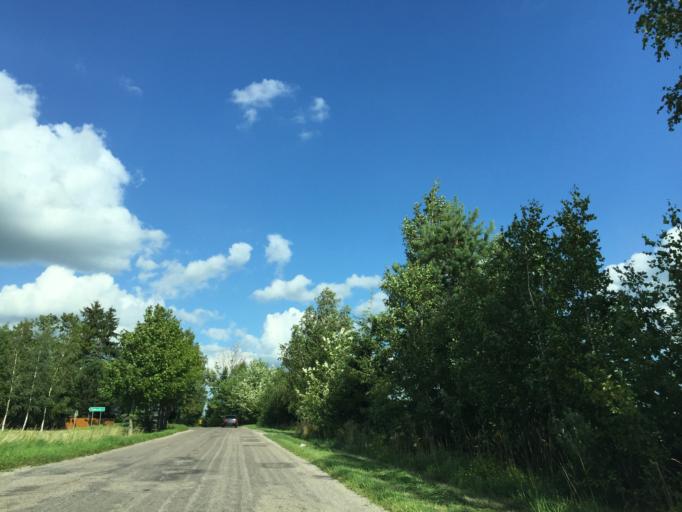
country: PL
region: Podlasie
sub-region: Powiat sejnenski
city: Punsk
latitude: 54.2256
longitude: 23.1005
